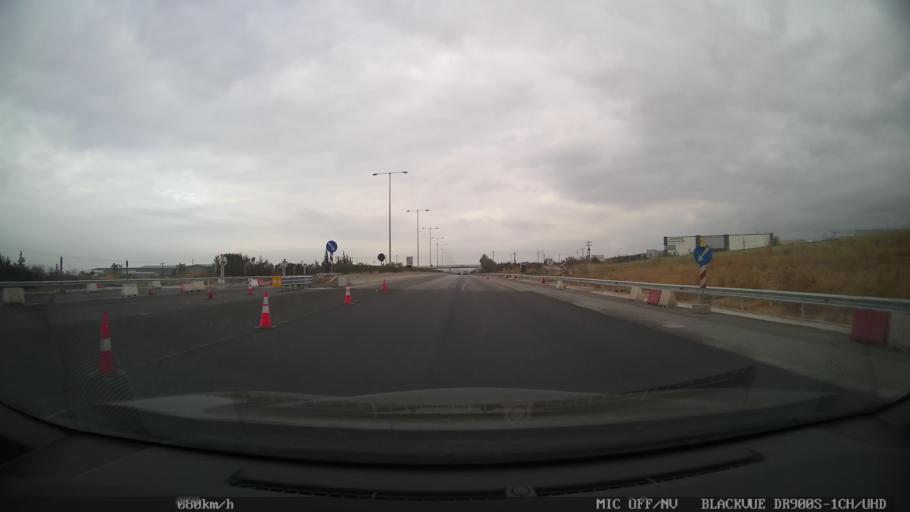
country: GR
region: Central Macedonia
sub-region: Nomos Thessalonikis
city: Evosmos
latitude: 40.6963
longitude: 22.8931
